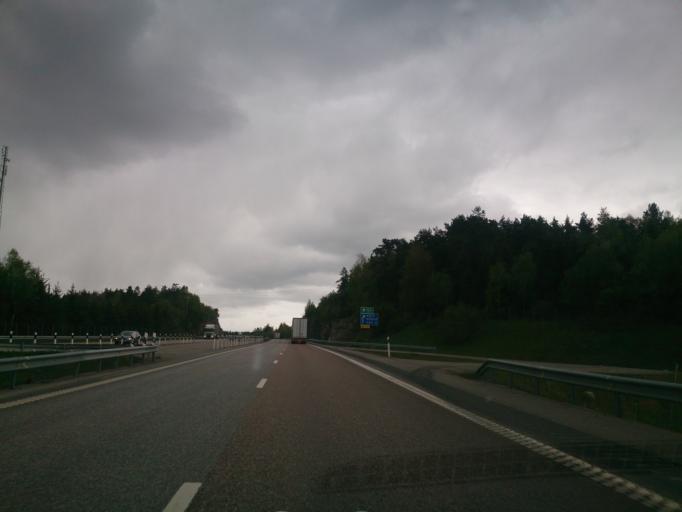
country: SE
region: Soedermanland
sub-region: Trosa Kommun
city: Vagnharad
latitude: 59.0164
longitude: 17.5495
